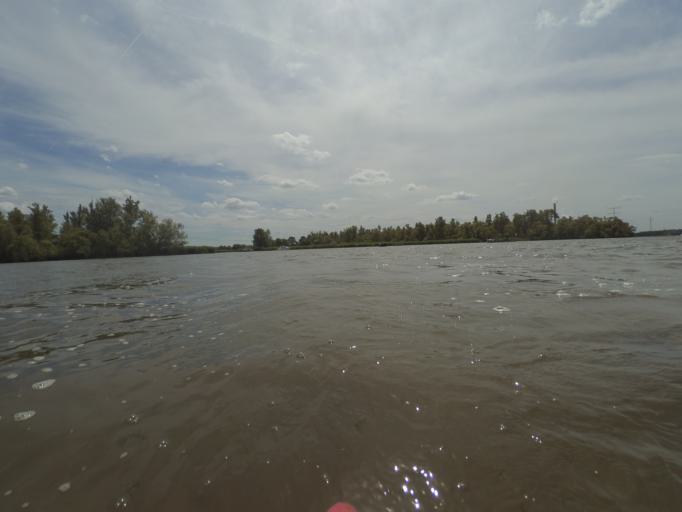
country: NL
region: North Brabant
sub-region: Gemeente Geertruidenberg
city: Geertruidenberg
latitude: 51.7270
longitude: 4.8488
